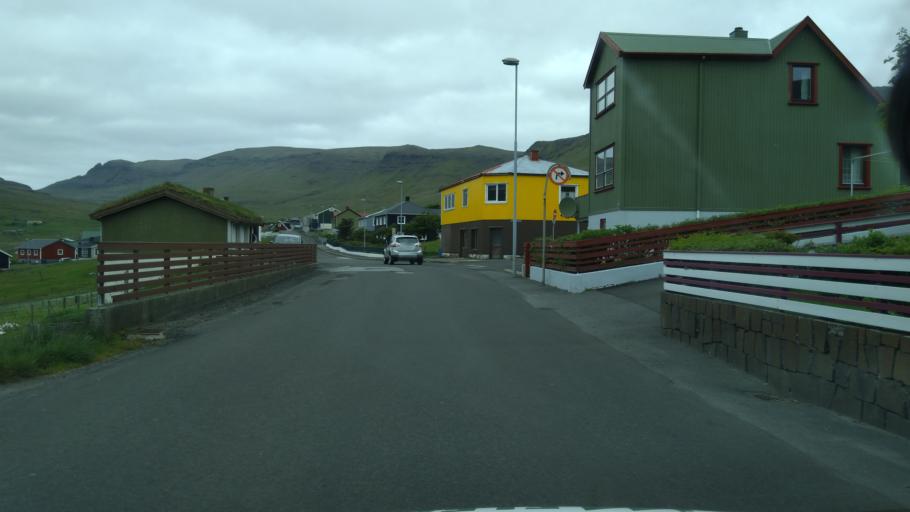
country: FO
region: Suduroy
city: Tvoroyri
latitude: 61.5630
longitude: -6.8364
